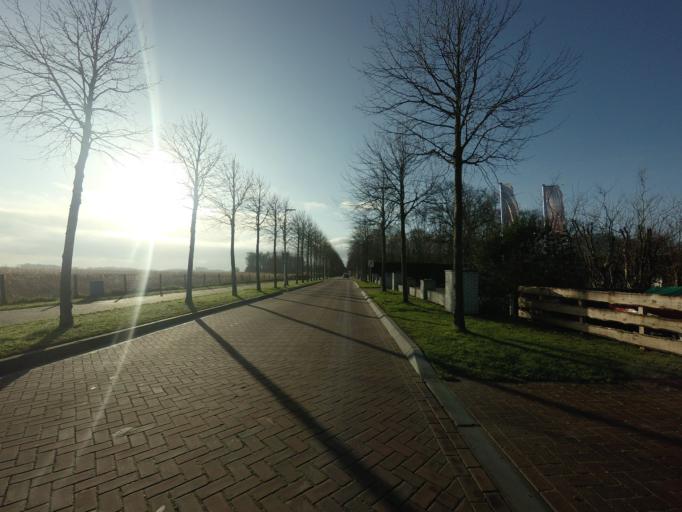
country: NL
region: North Holland
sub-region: Gemeente Texel
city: Den Burg
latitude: 53.1536
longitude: 4.8684
